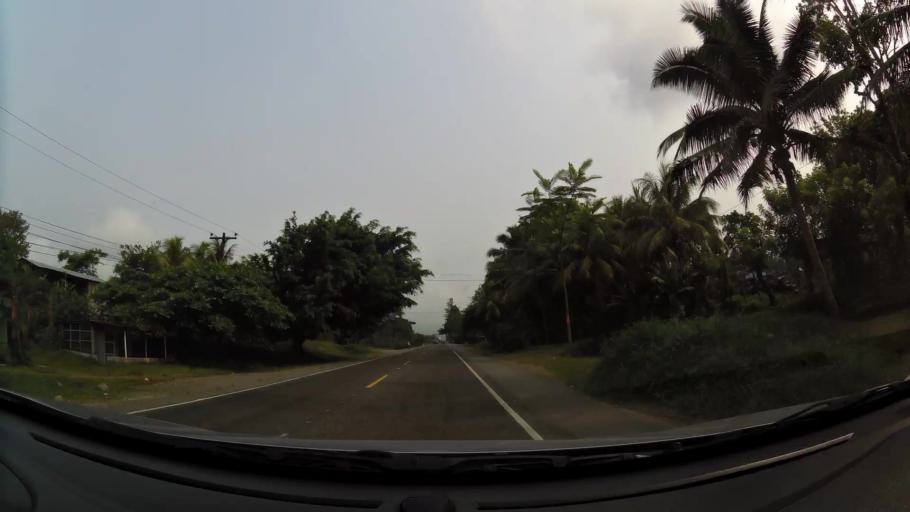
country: HN
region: Atlantida
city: Mezapa
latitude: 15.6047
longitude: -87.6114
